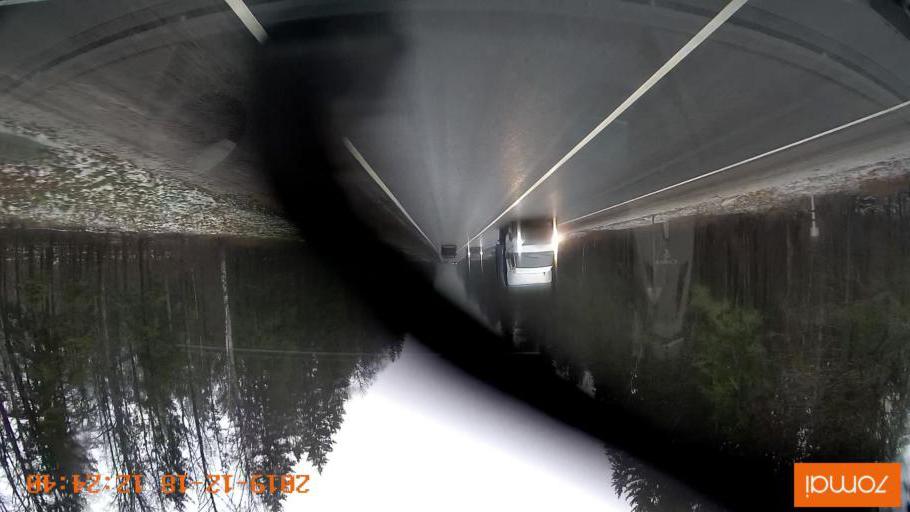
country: RU
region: Moskovskaya
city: Novopetrovskoye
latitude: 56.0275
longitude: 36.5009
